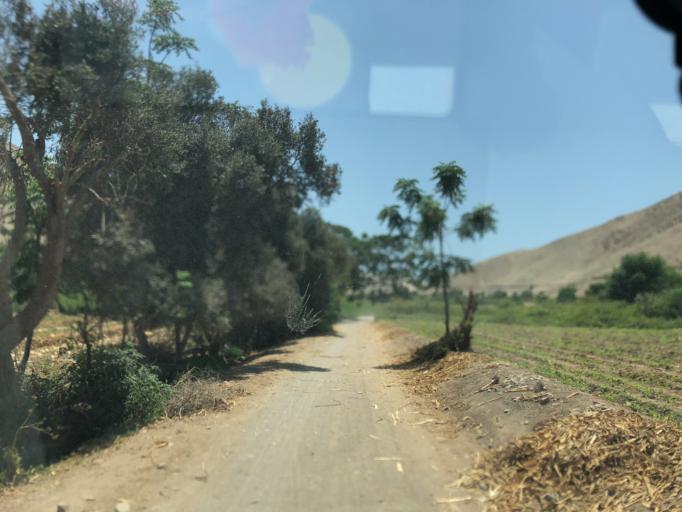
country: PE
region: Lima
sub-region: Provincia de Canete
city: Quilmana
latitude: -12.9845
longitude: -76.4331
